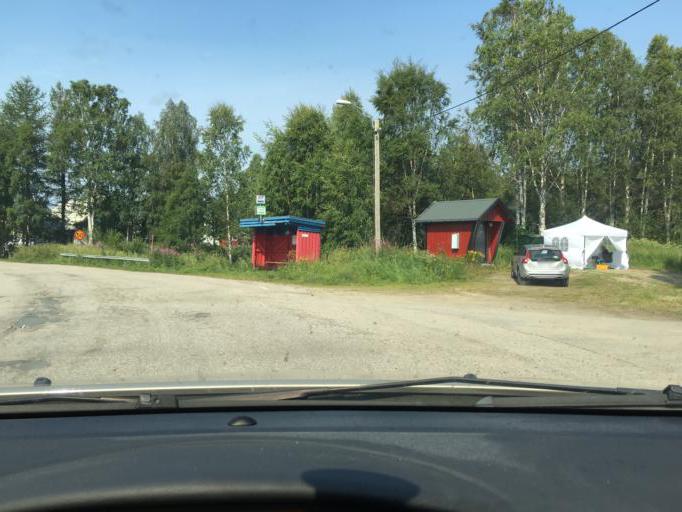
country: SE
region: Norrbotten
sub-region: Kalix Kommun
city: Kalix
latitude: 65.7932
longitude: 23.1746
